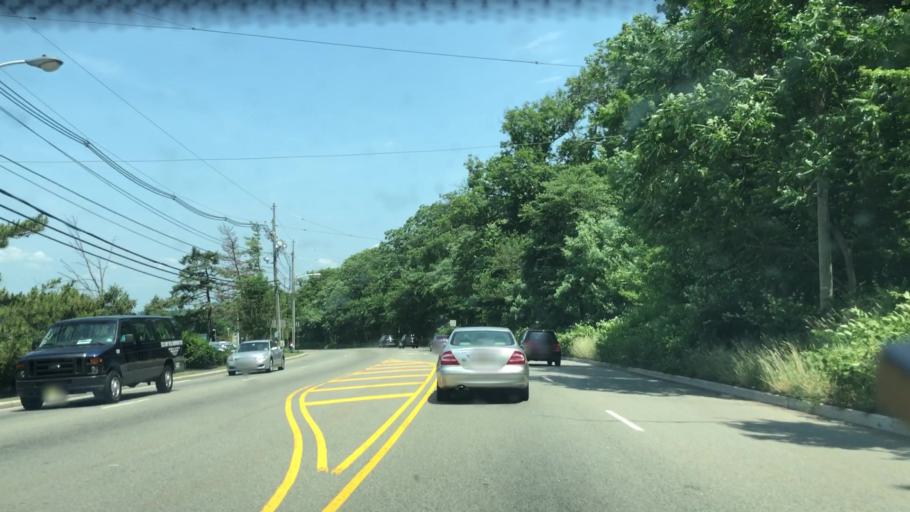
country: US
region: New Jersey
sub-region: Essex County
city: West Orange
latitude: 40.8035
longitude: -74.2473
